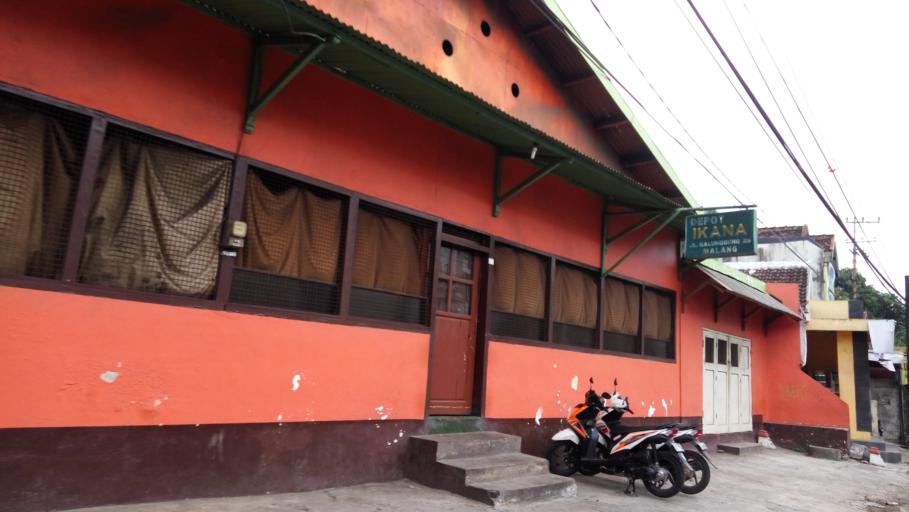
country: ID
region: East Java
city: Malang
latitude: -7.9706
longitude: 112.6135
